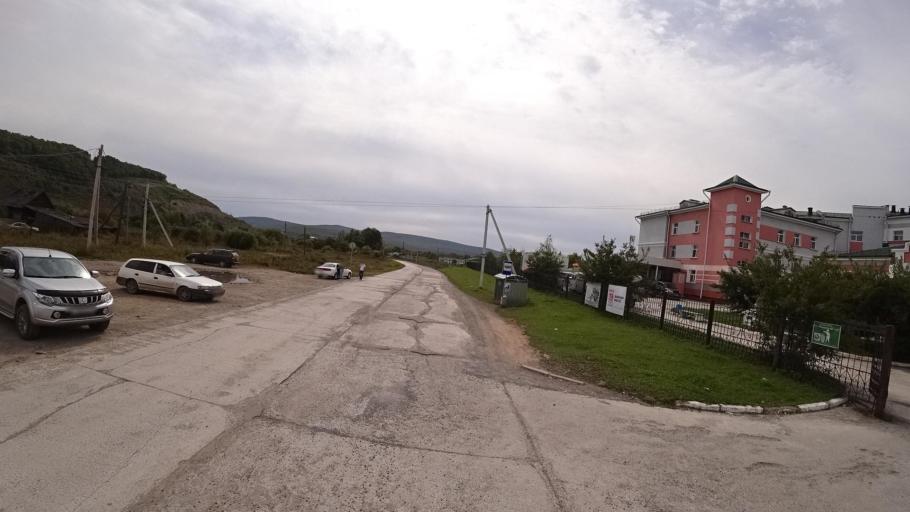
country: RU
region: Jewish Autonomous Oblast
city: Khingansk
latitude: 48.9965
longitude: 131.0510
